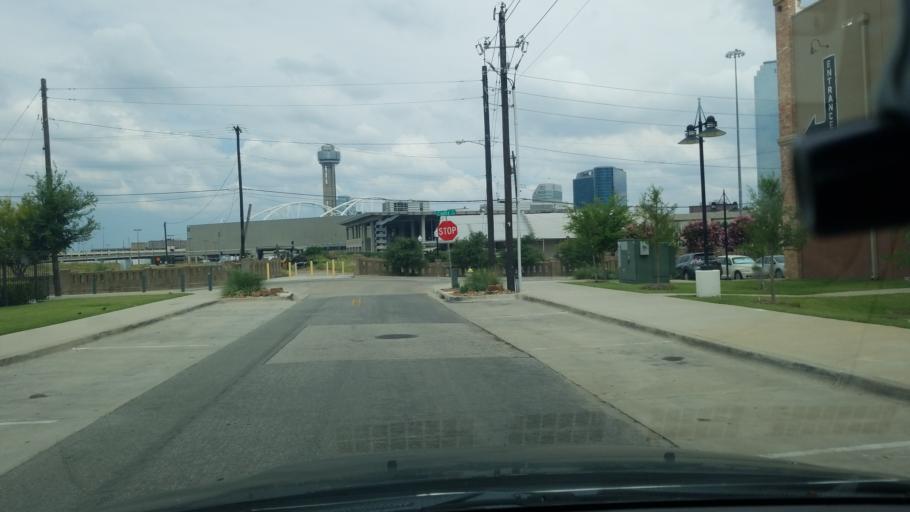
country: US
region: Texas
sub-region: Dallas County
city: Dallas
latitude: 32.7694
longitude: -96.7998
